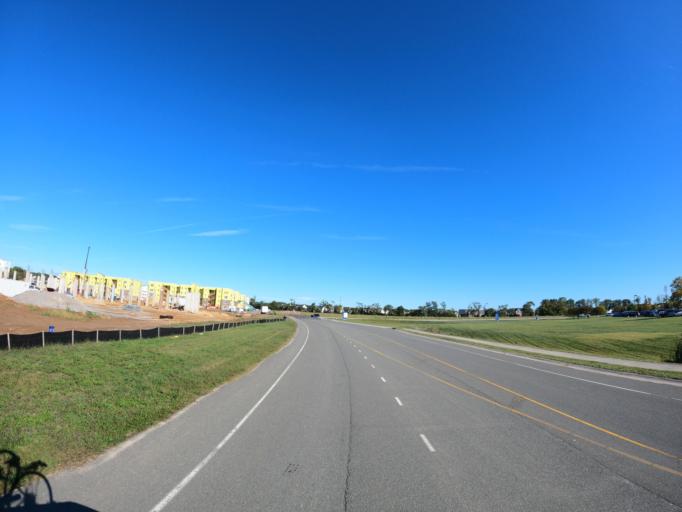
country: US
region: Delaware
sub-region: Sussex County
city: Lewes
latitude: 38.7262
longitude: -75.1376
